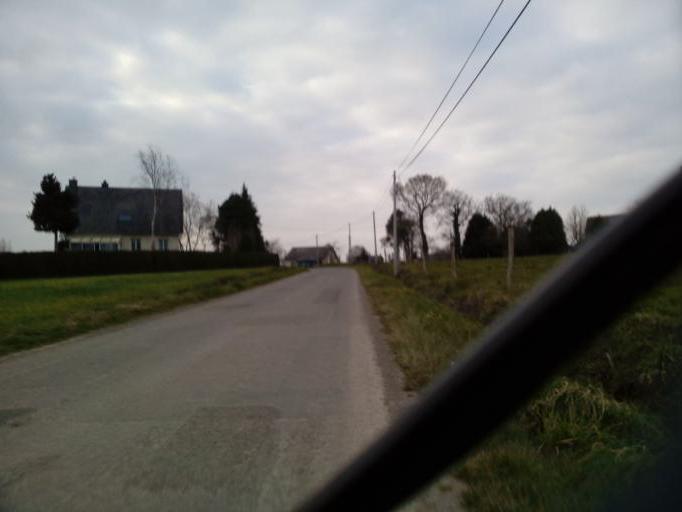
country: FR
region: Brittany
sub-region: Departement d'Ille-et-Vilaine
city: Cintre
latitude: 48.1090
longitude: -1.8966
